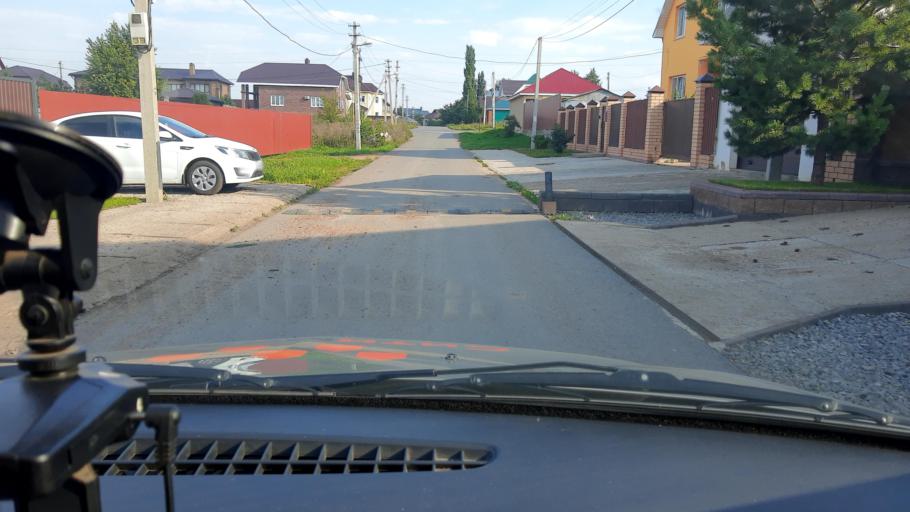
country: RU
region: Bashkortostan
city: Ufa
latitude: 54.5982
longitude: 55.9310
